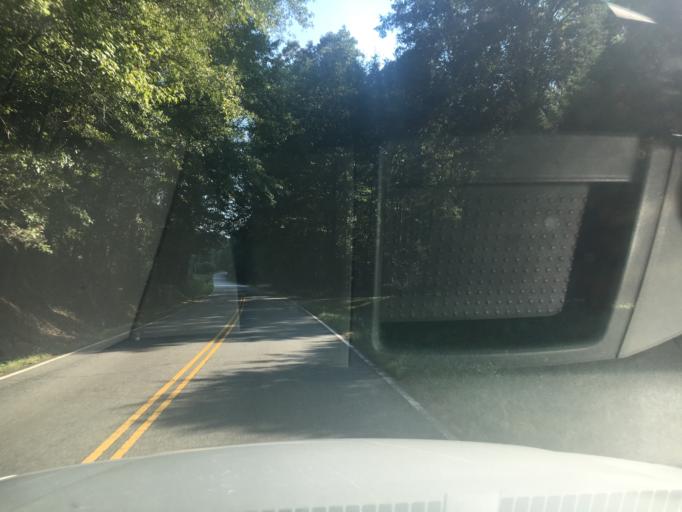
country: US
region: South Carolina
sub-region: Pickens County
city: Liberty
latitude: 34.7123
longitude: -82.6387
